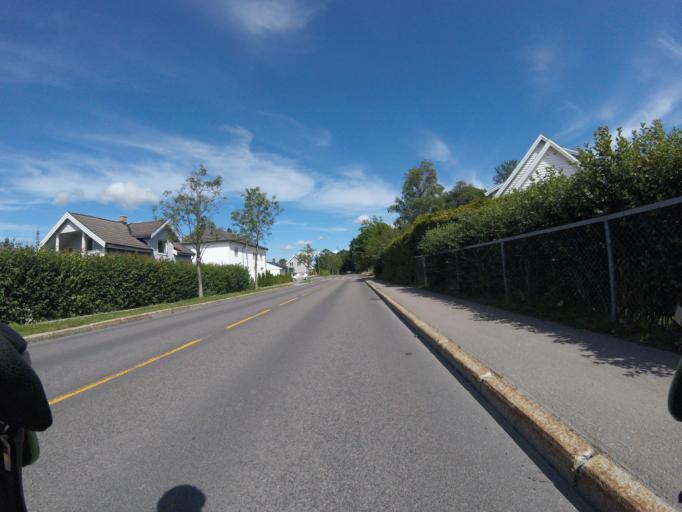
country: NO
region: Akershus
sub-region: Skedsmo
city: Lillestrom
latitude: 59.9439
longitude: 11.0173
